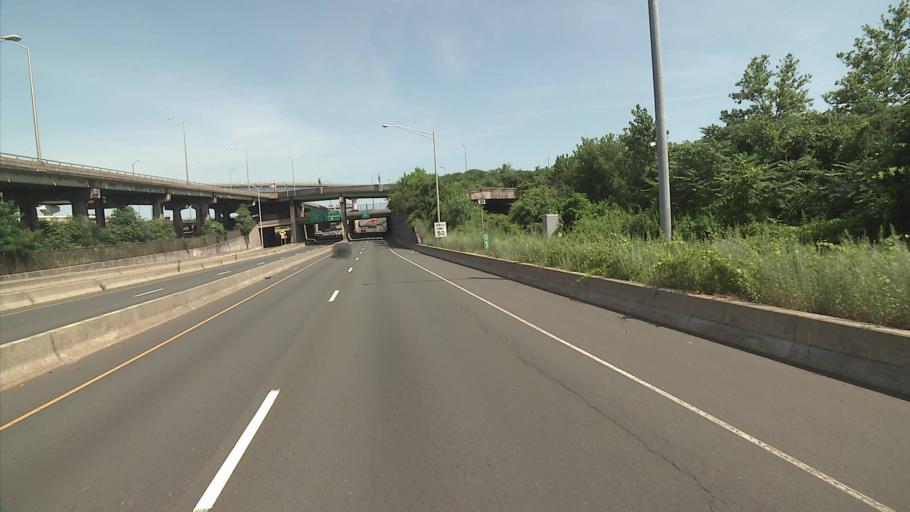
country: US
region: Connecticut
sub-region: Hartford County
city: Hartford
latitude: 41.7681
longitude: -72.6679
